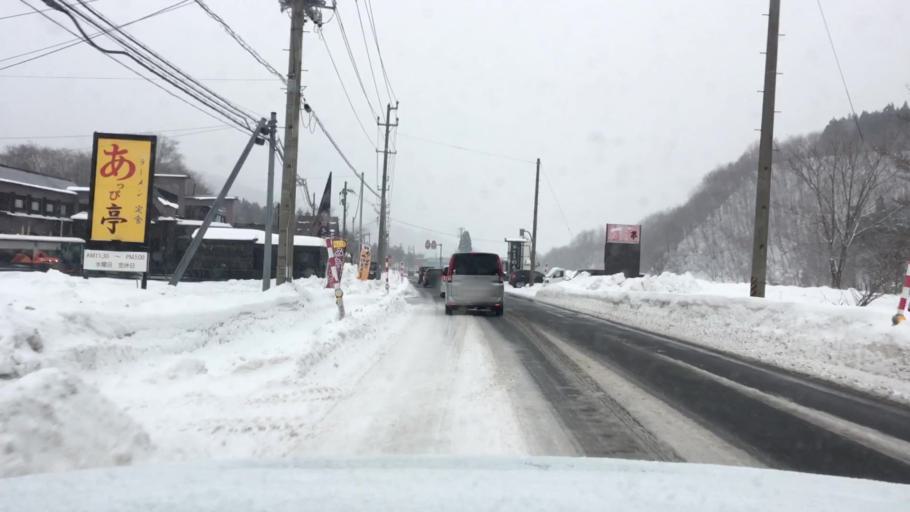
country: JP
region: Akita
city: Hanawa
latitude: 40.0428
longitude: 140.9983
